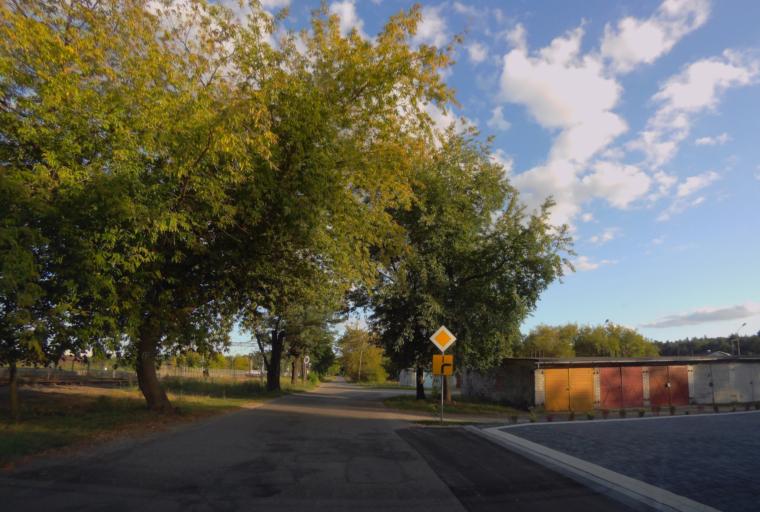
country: PL
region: Subcarpathian Voivodeship
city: Nowa Sarzyna
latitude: 50.3206
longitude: 22.3473
